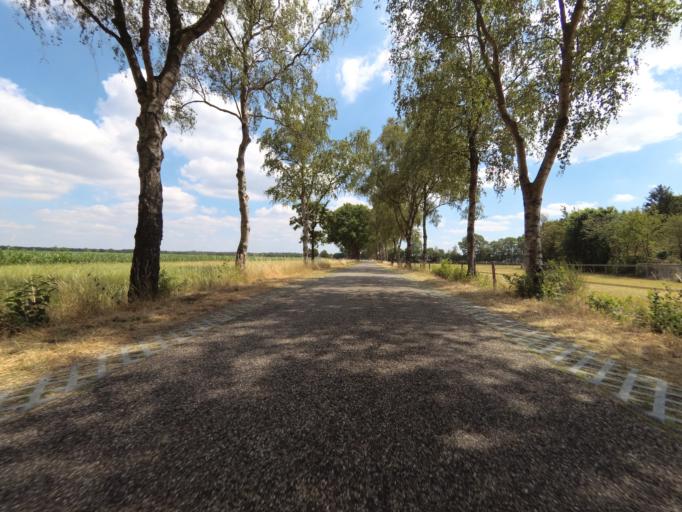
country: NL
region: Overijssel
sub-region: Gemeente Raalte
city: Raalte
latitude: 52.3308
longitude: 6.3489
